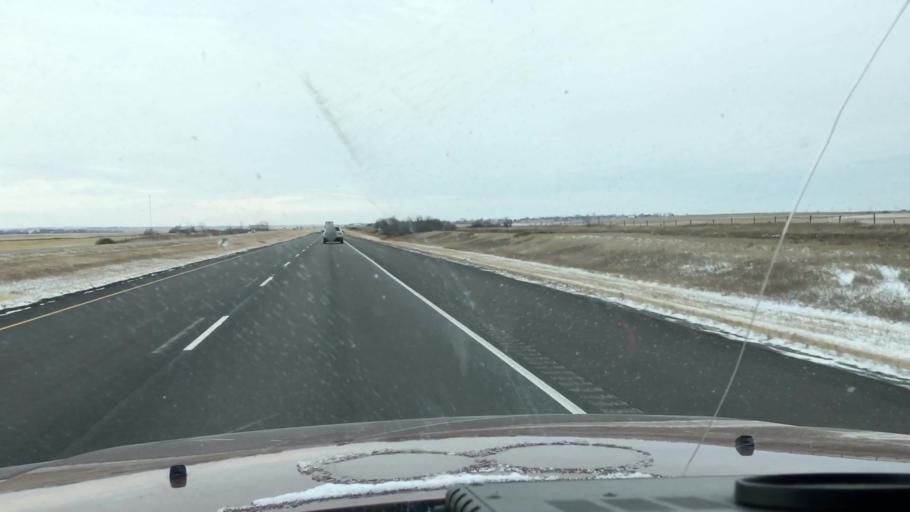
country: CA
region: Saskatchewan
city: Saskatoon
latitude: 51.8357
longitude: -106.5033
